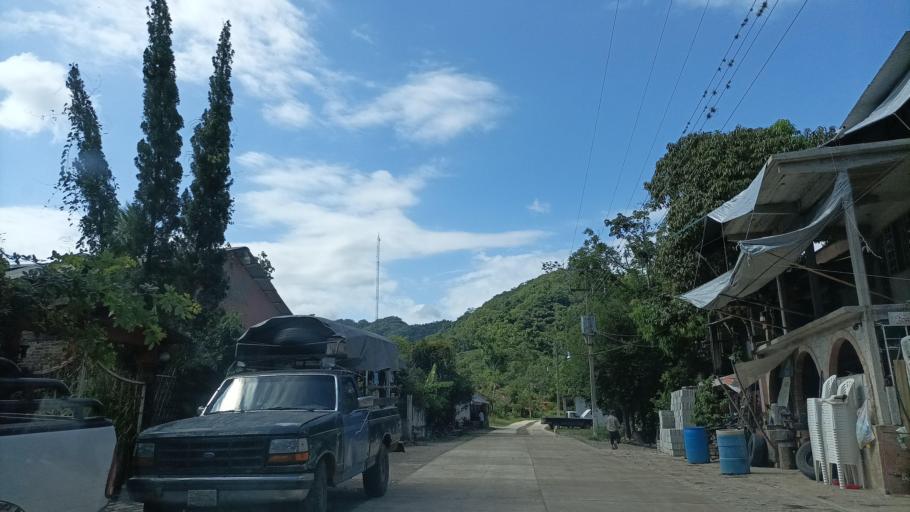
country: MX
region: Hidalgo
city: Huautla
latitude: 21.1327
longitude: -98.2506
